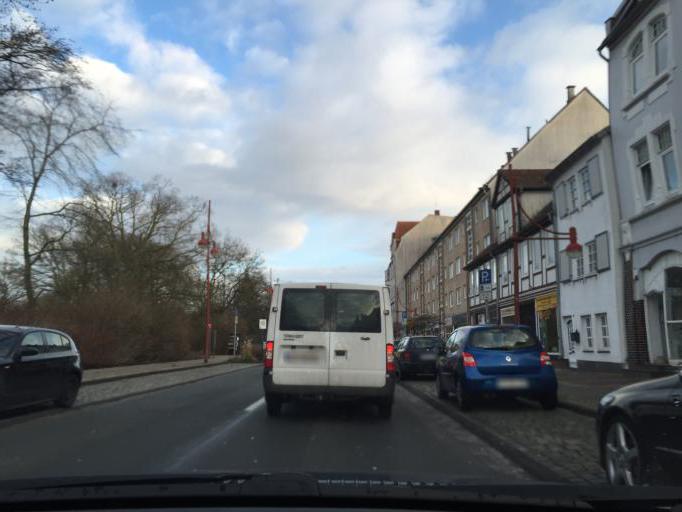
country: DE
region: Lower Saxony
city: Celle
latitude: 52.6213
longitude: 10.0687
